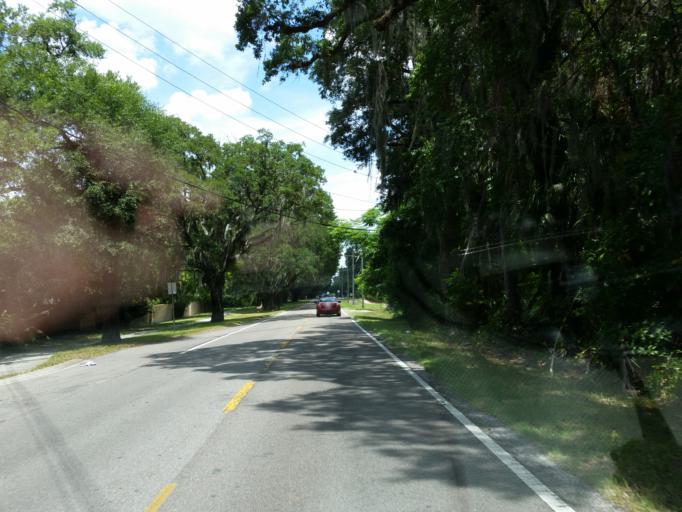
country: US
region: Florida
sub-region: Hillsborough County
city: Valrico
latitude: 27.9576
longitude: -82.2528
